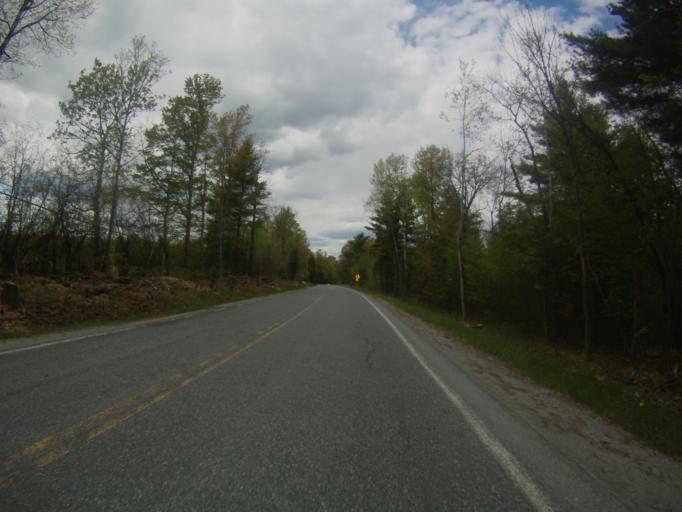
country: US
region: New York
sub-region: Essex County
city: Port Henry
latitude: 44.0067
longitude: -73.4986
